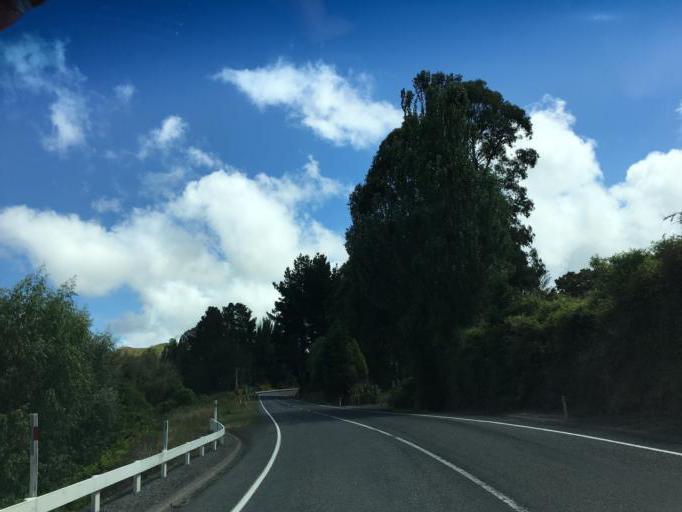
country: NZ
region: Hawke's Bay
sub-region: Wairoa District
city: Wairoa
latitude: -39.0620
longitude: 177.0402
